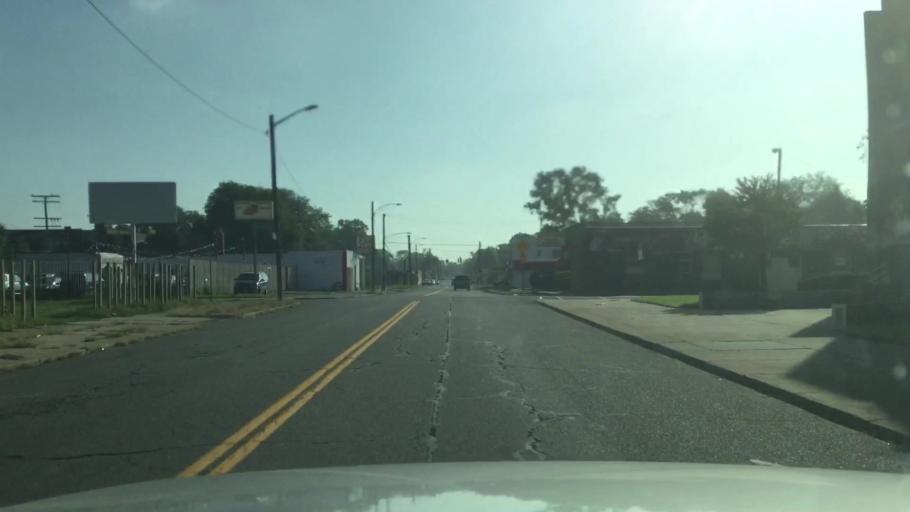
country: US
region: Michigan
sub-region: Oakland County
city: Hazel Park
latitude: 42.4398
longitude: -83.0934
